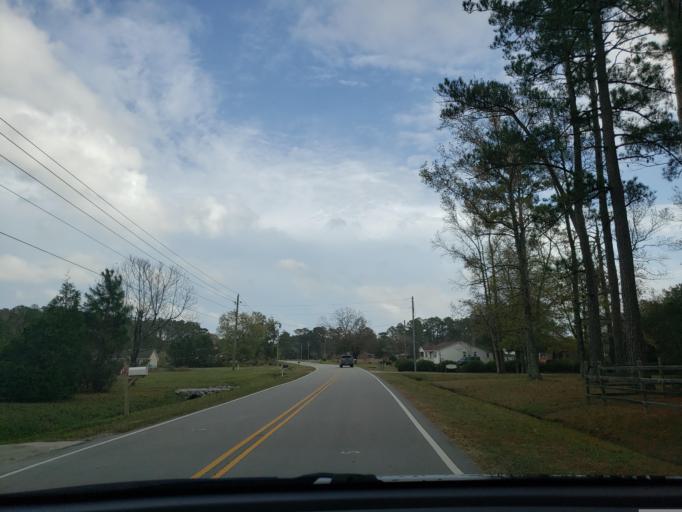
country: US
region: North Carolina
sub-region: Onslow County
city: Jacksonville
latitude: 34.6959
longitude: -77.5579
